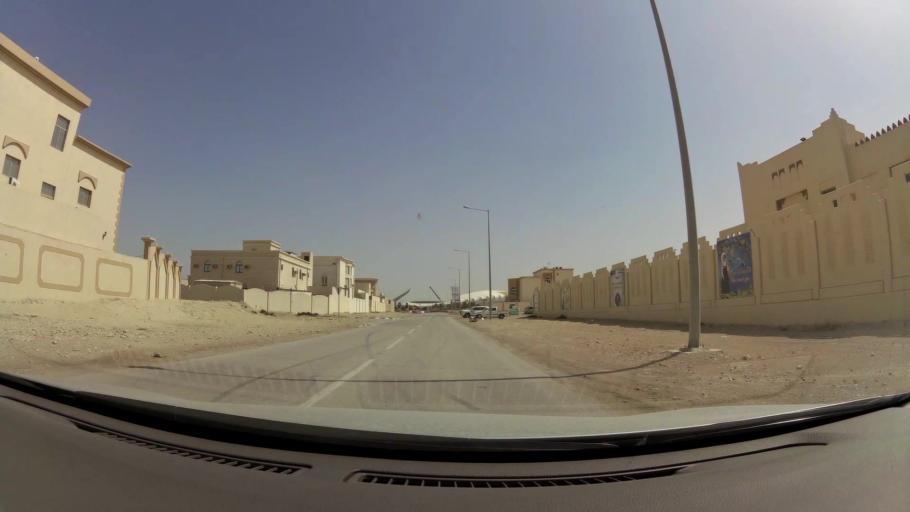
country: QA
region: Baladiyat Umm Salal
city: Umm Salal Muhammad
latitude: 25.3780
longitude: 51.4661
